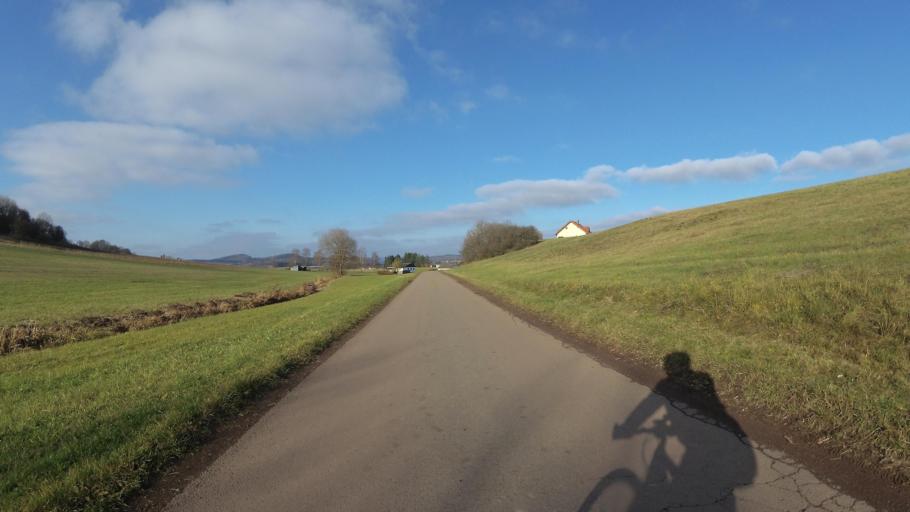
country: DE
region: Rheinland-Pfalz
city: Hahnweiler
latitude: 49.5433
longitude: 7.1932
